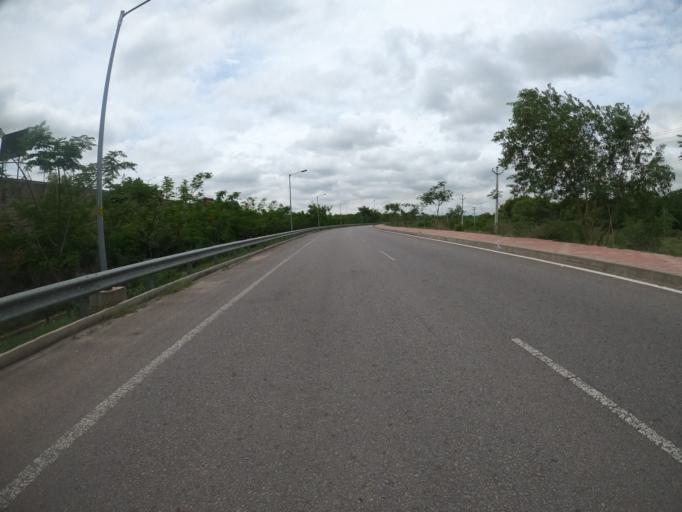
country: IN
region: Telangana
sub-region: Rangareddi
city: Sriramnagar
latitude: 17.2540
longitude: 78.3758
